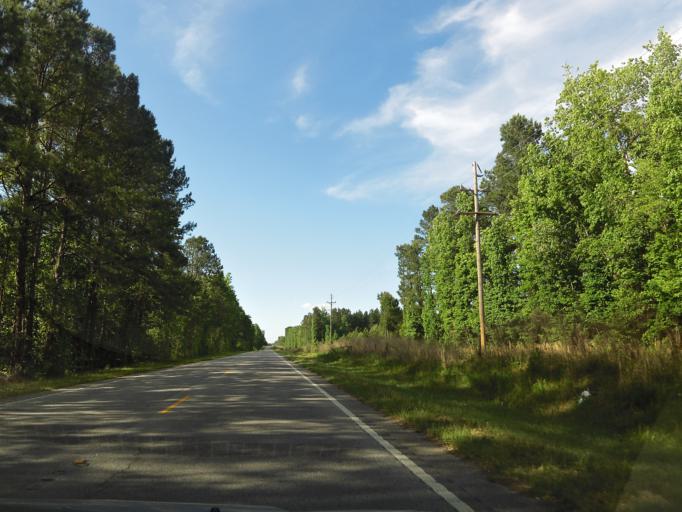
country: US
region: South Carolina
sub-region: Allendale County
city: Fairfax
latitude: 32.9111
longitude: -81.2376
